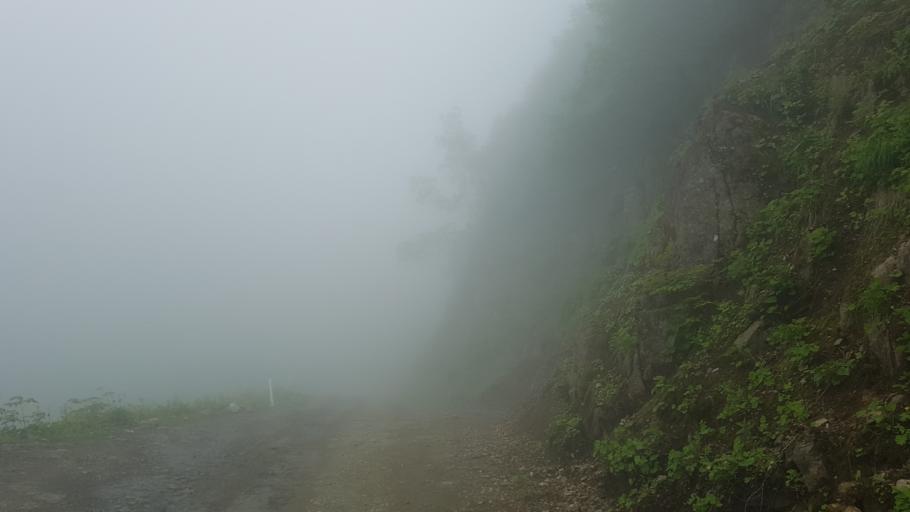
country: GE
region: Guria
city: Ozurgeti
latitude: 41.8297
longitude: 42.1512
